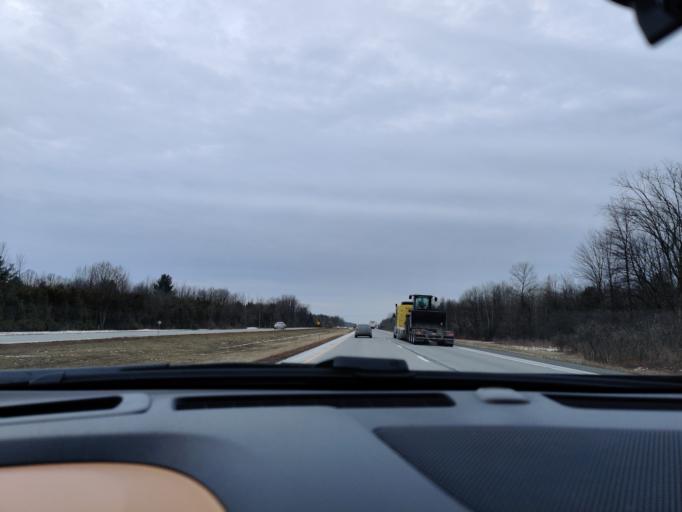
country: US
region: New York
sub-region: St. Lawrence County
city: Ogdensburg
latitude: 44.8184
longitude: -75.3933
